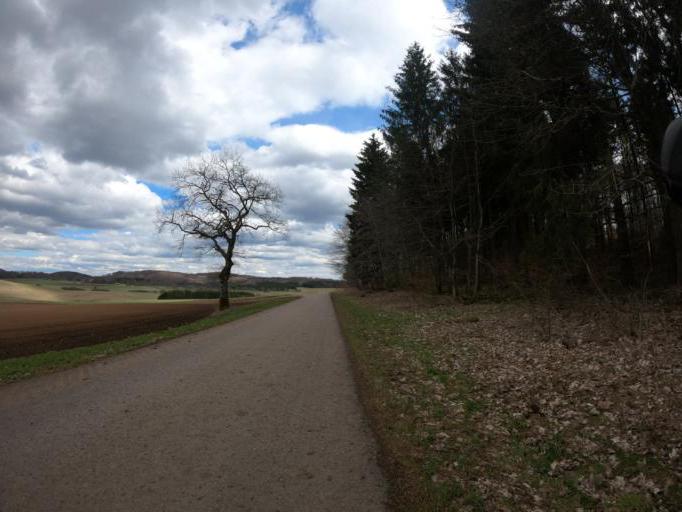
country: DE
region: Baden-Wuerttemberg
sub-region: Tuebingen Region
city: Trochtelfingen
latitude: 48.3798
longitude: 9.2017
